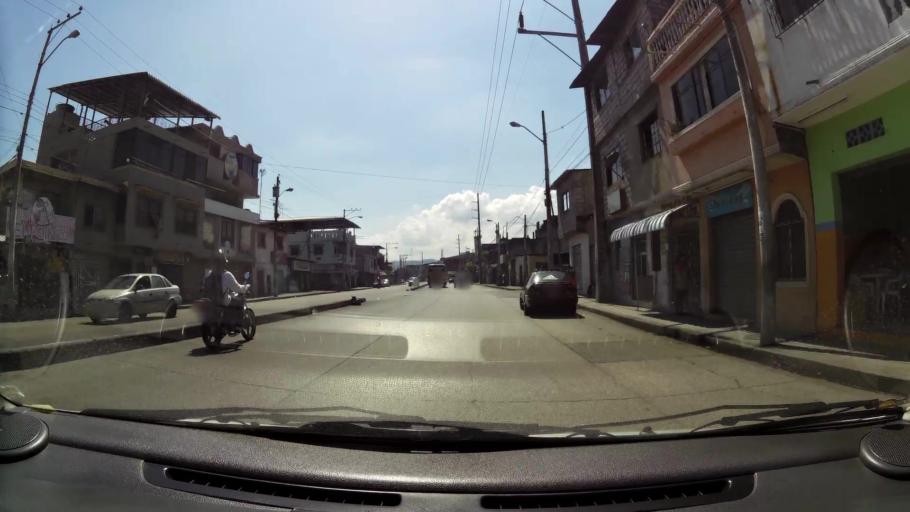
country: EC
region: Guayas
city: Guayaquil
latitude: -2.2294
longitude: -79.9410
